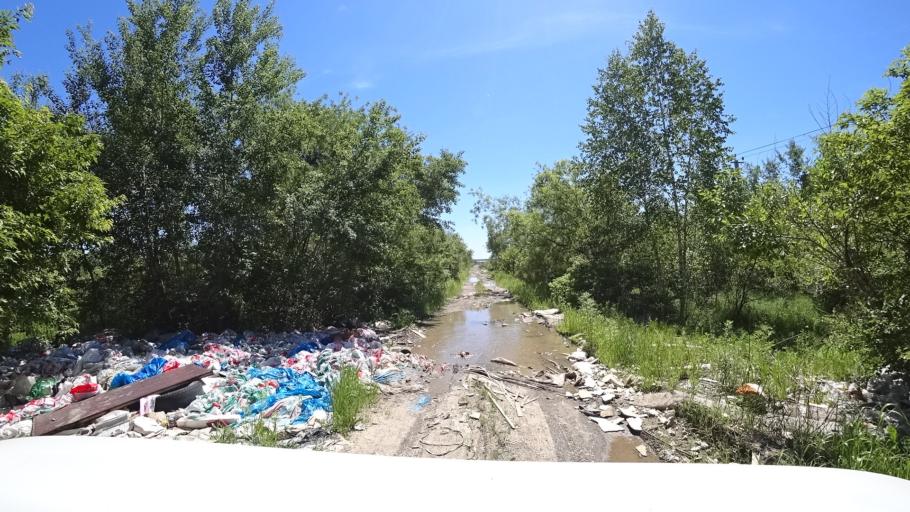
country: RU
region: Khabarovsk Krai
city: Topolevo
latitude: 48.4870
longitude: 135.1769
